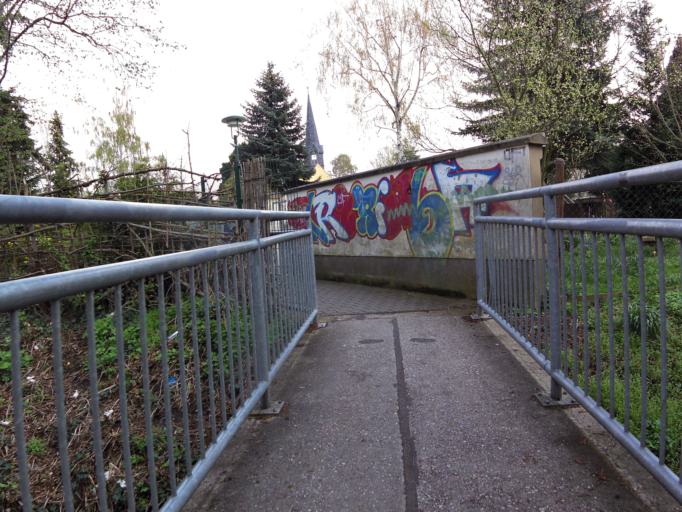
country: DE
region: Saxony
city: Markranstadt
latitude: 51.3222
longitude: 12.2589
